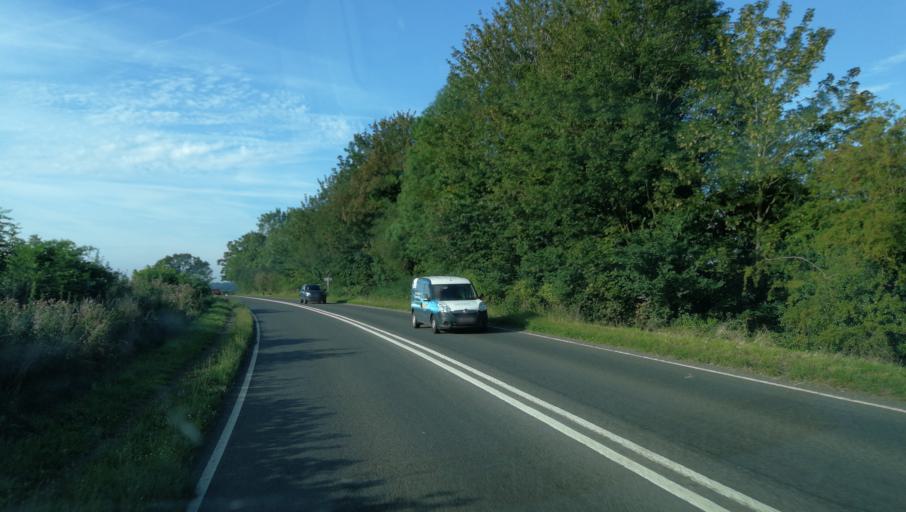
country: GB
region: England
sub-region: Oxfordshire
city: Adderbury
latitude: 52.0073
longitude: -1.3168
